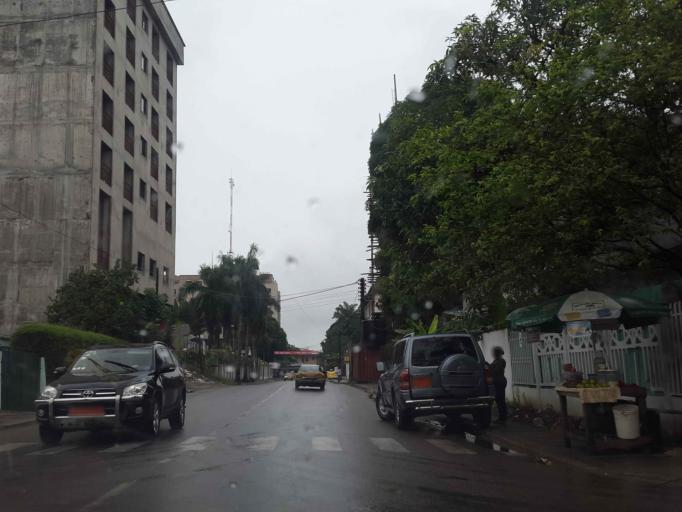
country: CM
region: Littoral
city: Douala
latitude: 4.0386
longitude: 9.6936
